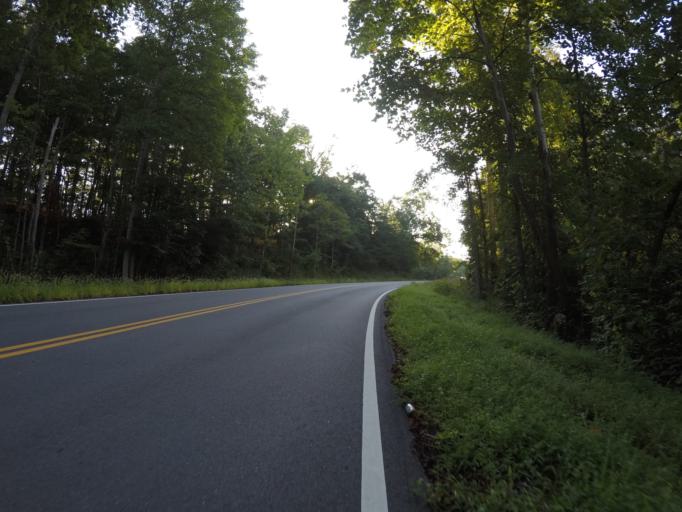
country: US
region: Ohio
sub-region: Lawrence County
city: Ironton
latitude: 38.6121
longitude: -82.6113
